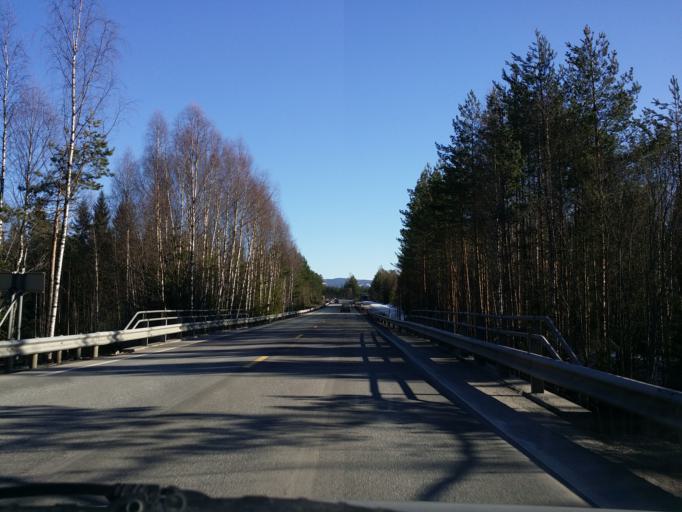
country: NO
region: Buskerud
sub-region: Ringerike
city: Honefoss
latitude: 60.2306
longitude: 10.2359
